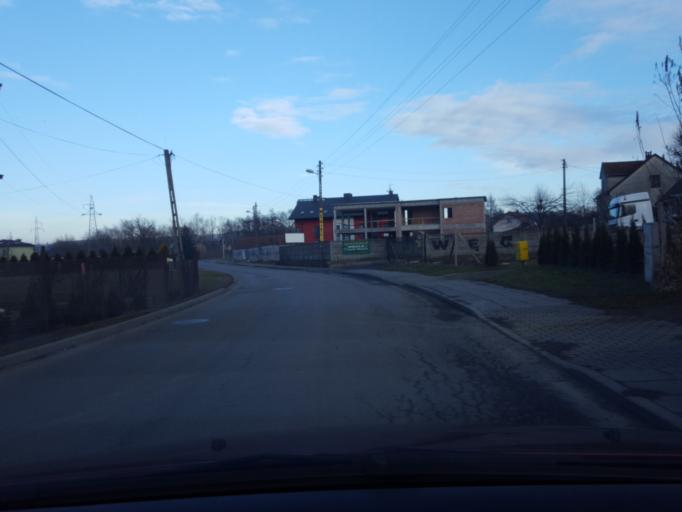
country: PL
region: Lesser Poland Voivodeship
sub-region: Powiat nowosadecki
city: Nowy Sacz
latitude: 49.5914
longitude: 20.6967
